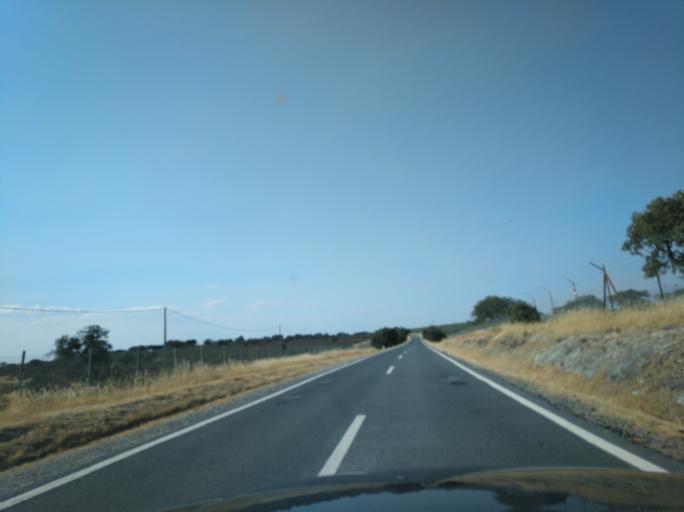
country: ES
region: Extremadura
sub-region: Provincia de Badajoz
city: Valencia del Mombuey
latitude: 38.1738
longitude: -7.2322
